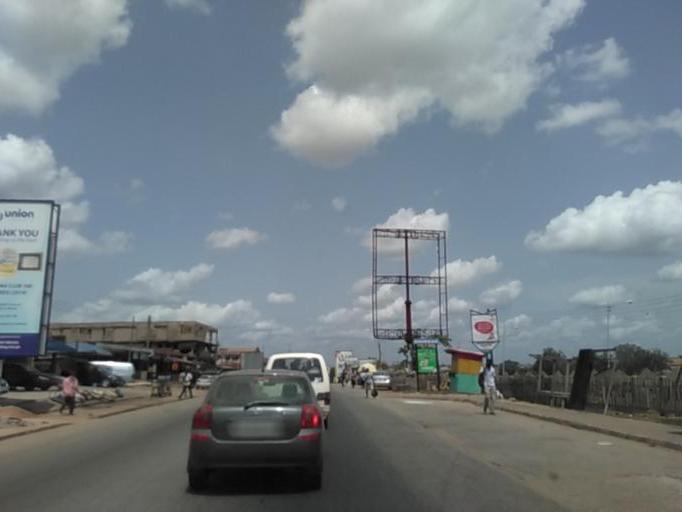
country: GH
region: Ashanti
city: Kumasi
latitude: 6.6626
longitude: -1.6012
